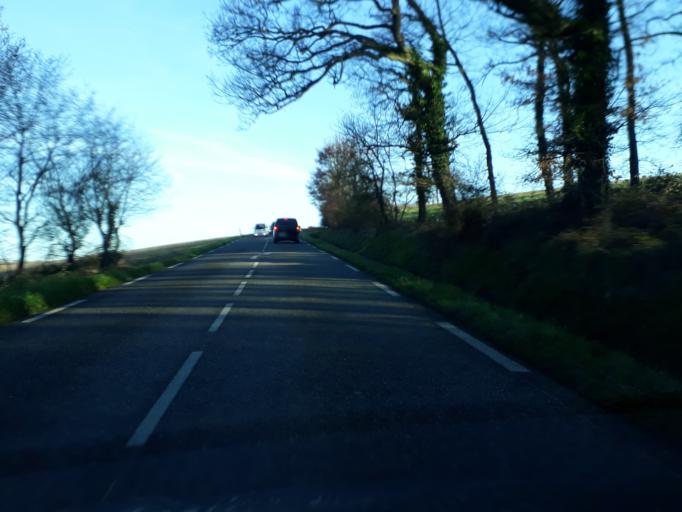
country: FR
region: Midi-Pyrenees
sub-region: Departement du Gers
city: Pujaudran
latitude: 43.5755
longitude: 1.1289
